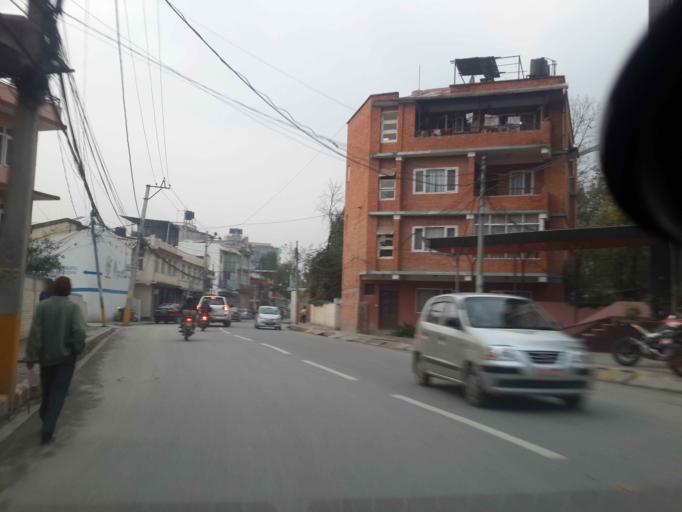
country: NP
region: Central Region
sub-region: Bagmati Zone
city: Kathmandu
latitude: 27.7209
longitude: 85.3316
